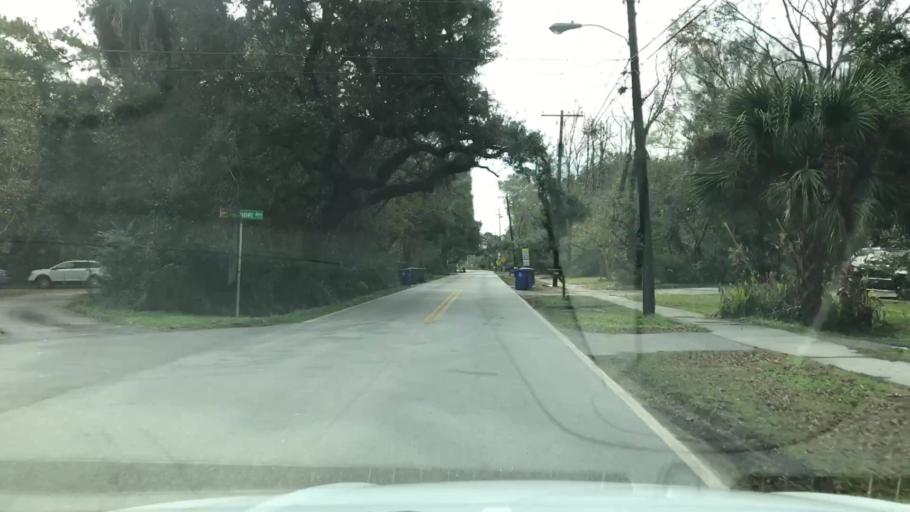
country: US
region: South Carolina
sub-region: Charleston County
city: North Charleston
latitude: 32.7807
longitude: -80.0198
